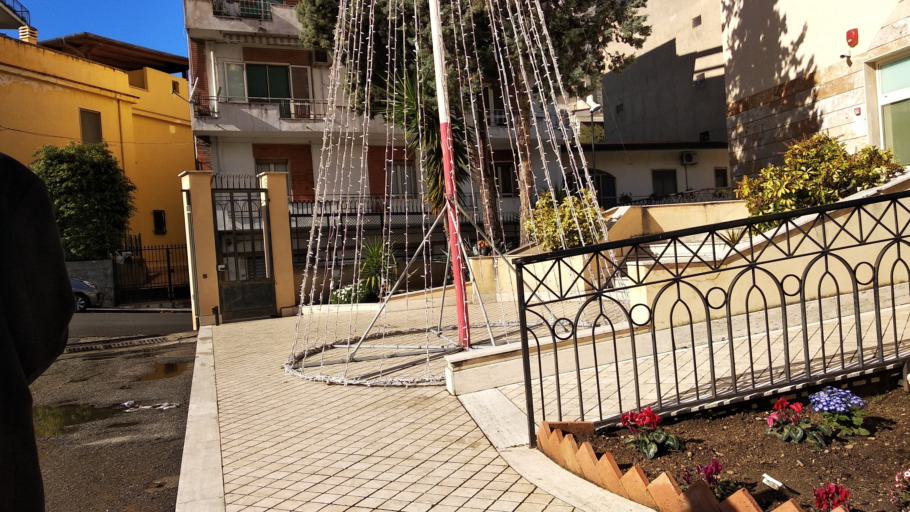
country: IT
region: Calabria
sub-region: Provincia di Reggio Calabria
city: Reggio Calabria
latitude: 38.1100
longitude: 15.6562
